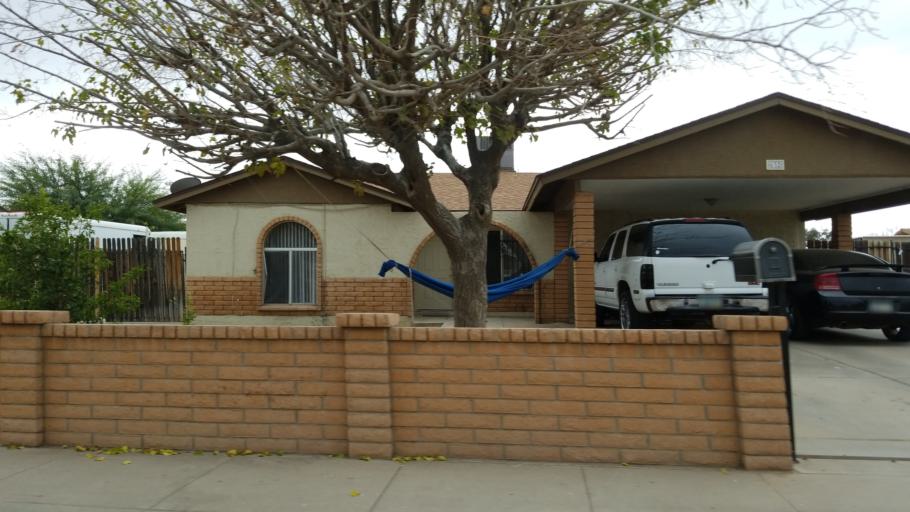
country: US
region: Arizona
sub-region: Maricopa County
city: Tolleson
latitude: 33.4566
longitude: -112.1893
